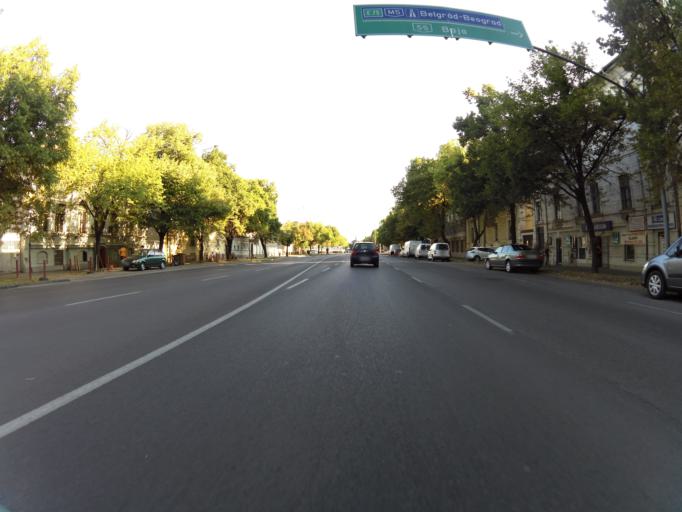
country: HU
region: Csongrad
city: Szeged
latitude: 46.2533
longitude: 20.1389
